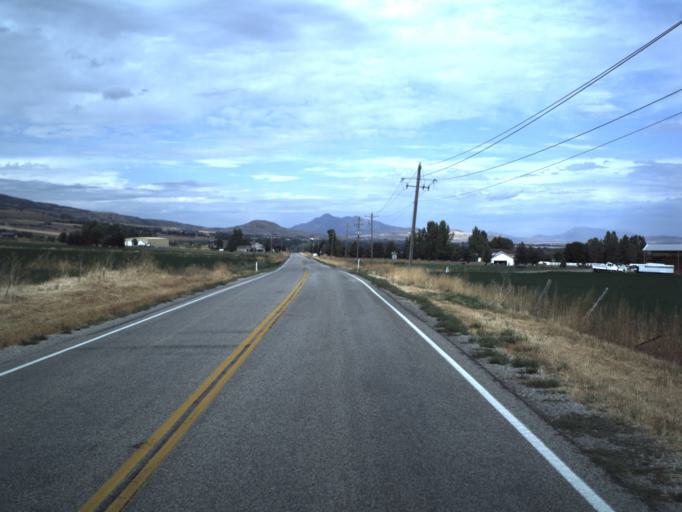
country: US
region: Utah
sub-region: Cache County
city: Wellsville
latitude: 41.6638
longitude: -111.9486
